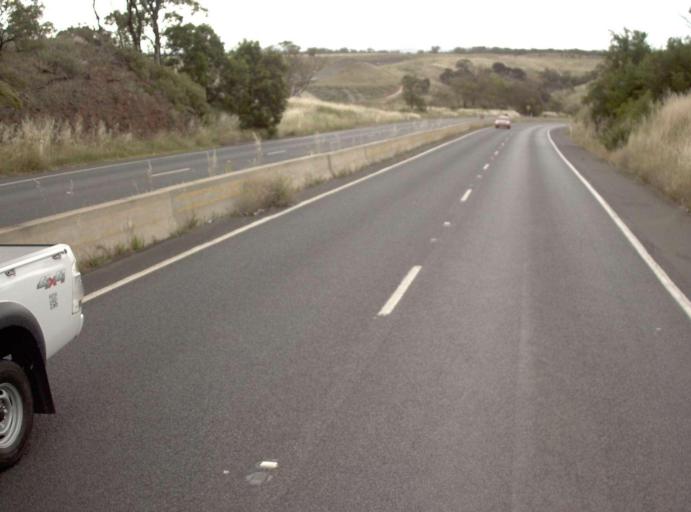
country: AU
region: Victoria
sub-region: Melton
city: Brookfield
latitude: -37.6873
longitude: 144.5214
